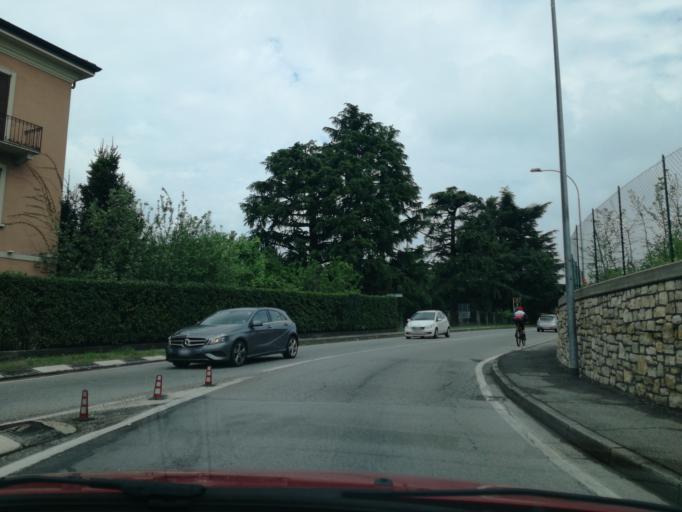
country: IT
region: Lombardy
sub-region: Provincia di Lecco
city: Canova-San Zeno
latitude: 45.7065
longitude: 9.4100
